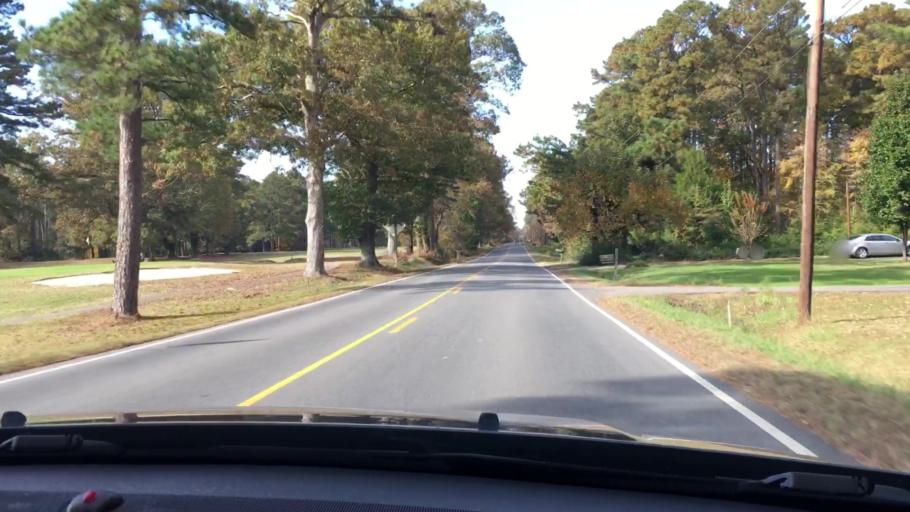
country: US
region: Virginia
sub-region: King William County
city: West Point
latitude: 37.5615
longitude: -76.8237
